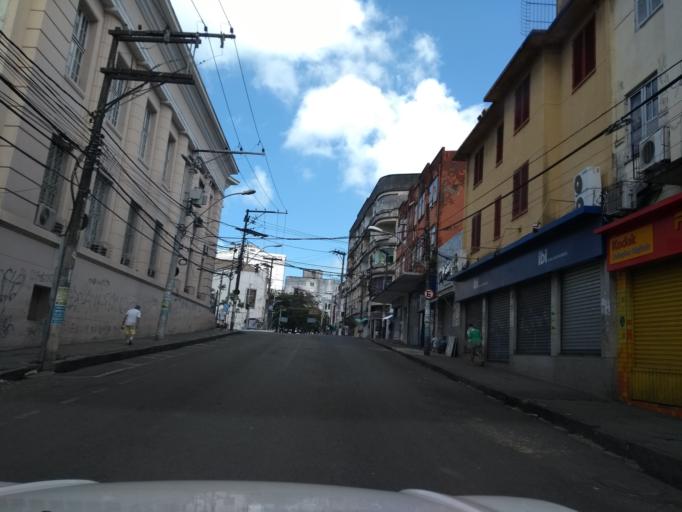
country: BR
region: Bahia
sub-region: Salvador
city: Salvador
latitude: -12.9821
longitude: -38.5138
